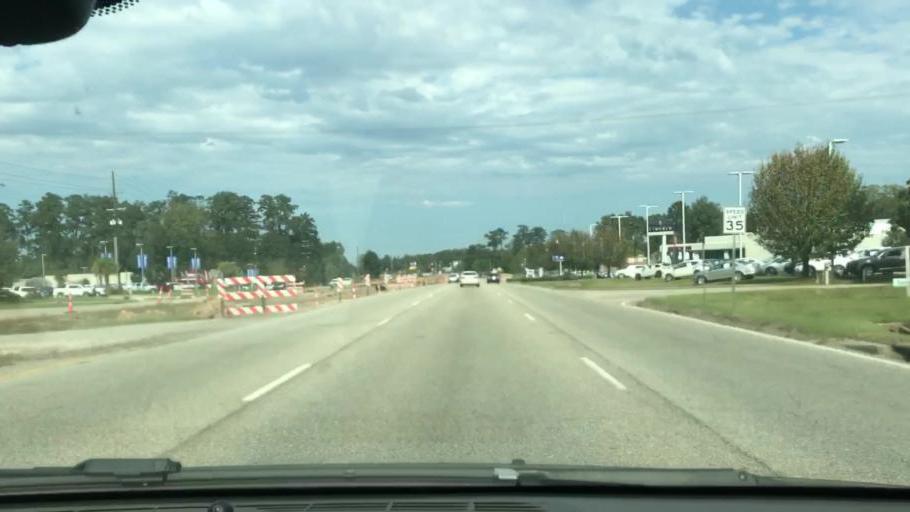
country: US
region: Louisiana
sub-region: Saint Tammany Parish
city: Covington
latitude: 30.4544
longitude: -90.0820
